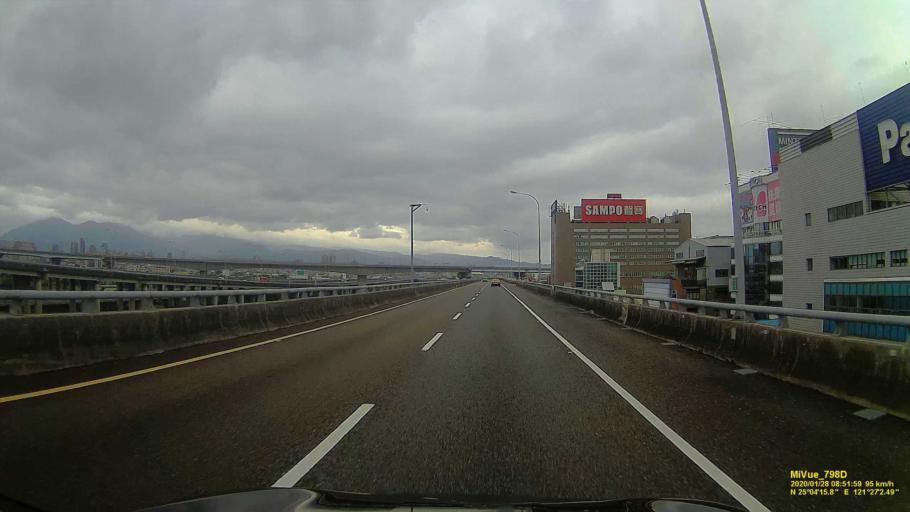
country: TW
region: Taipei
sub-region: Taipei
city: Banqiao
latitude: 25.0709
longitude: 121.4517
